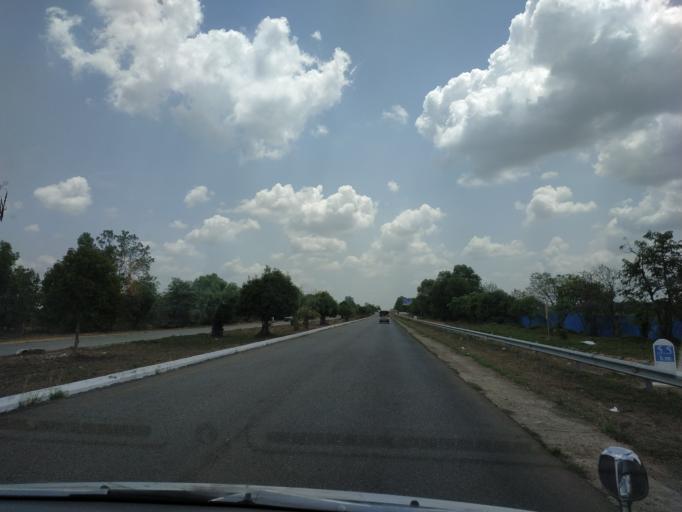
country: MM
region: Bago
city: Thanatpin
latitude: 17.1131
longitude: 96.1859
